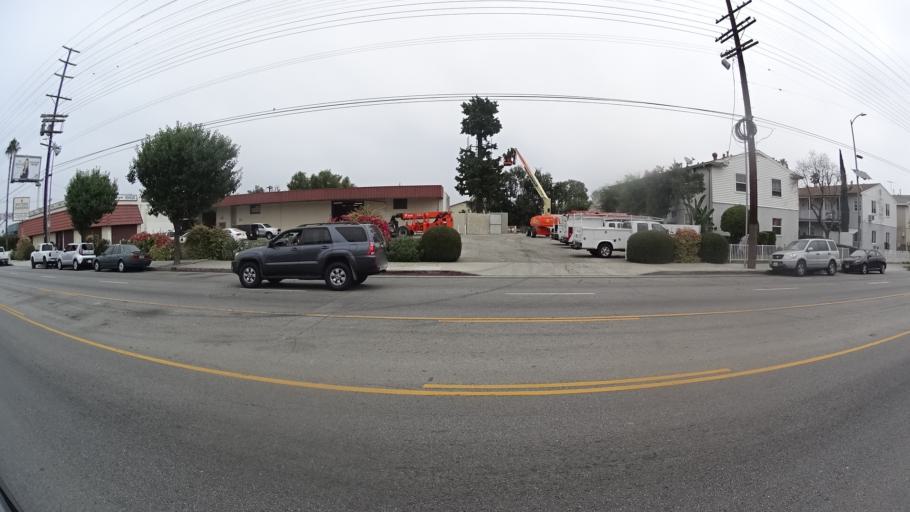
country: US
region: California
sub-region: Los Angeles County
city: Van Nuys
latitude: 34.1939
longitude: -118.4126
